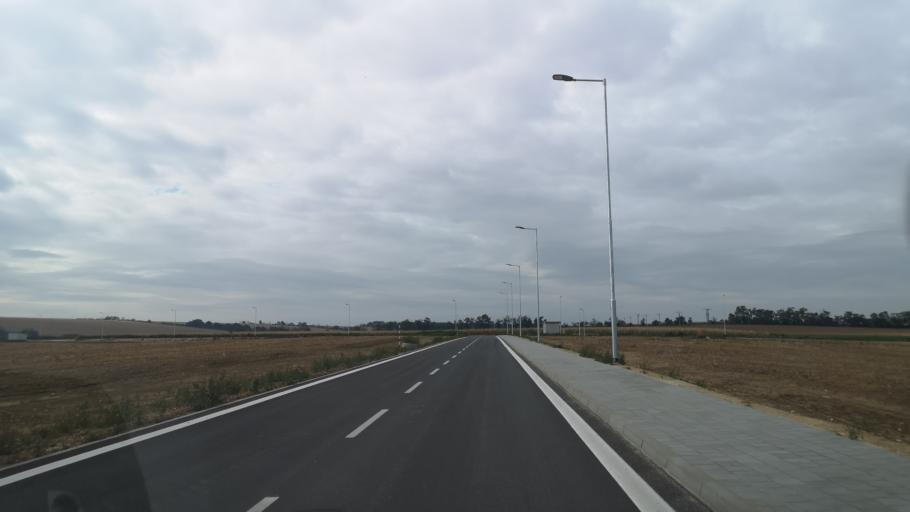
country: SK
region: Nitriansky
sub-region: Okres Nitra
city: Nitra
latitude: 48.3234
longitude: 18.0258
